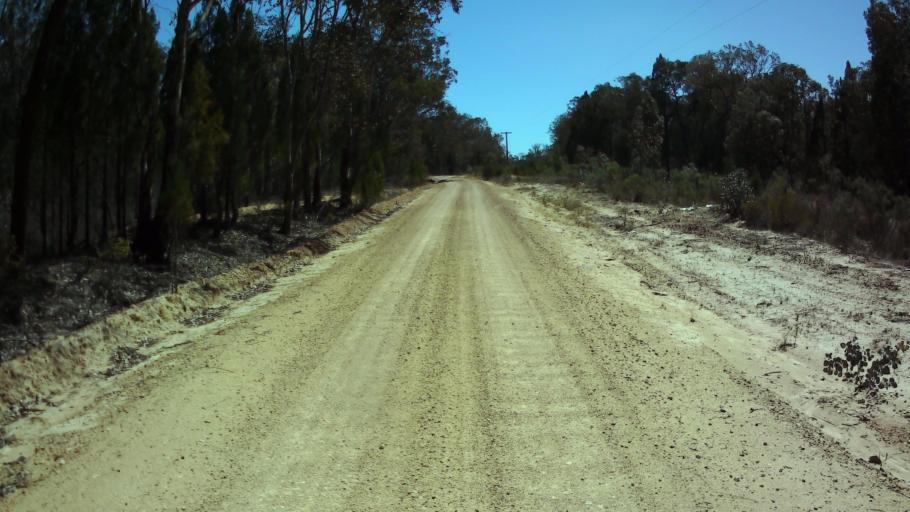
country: AU
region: New South Wales
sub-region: Cowra
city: Cowra
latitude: -33.8450
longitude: 148.4514
